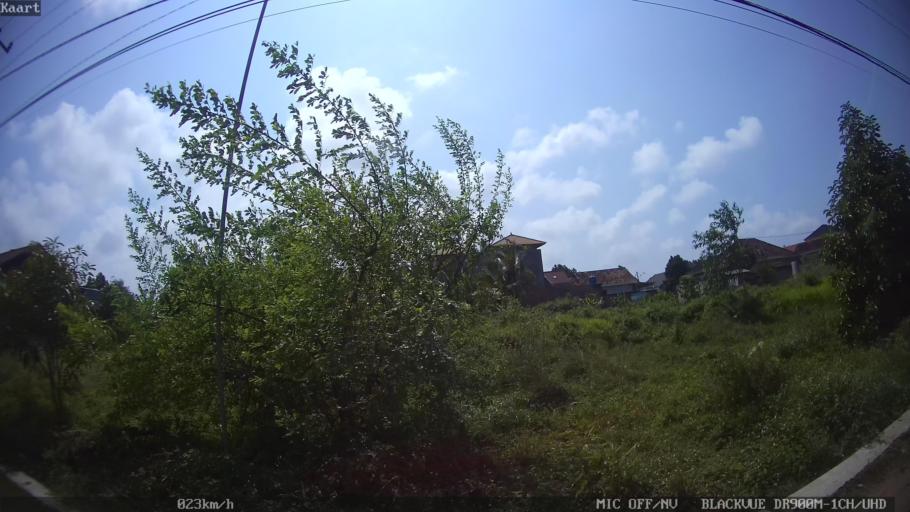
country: ID
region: Lampung
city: Kedaton
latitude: -5.3498
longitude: 105.2762
